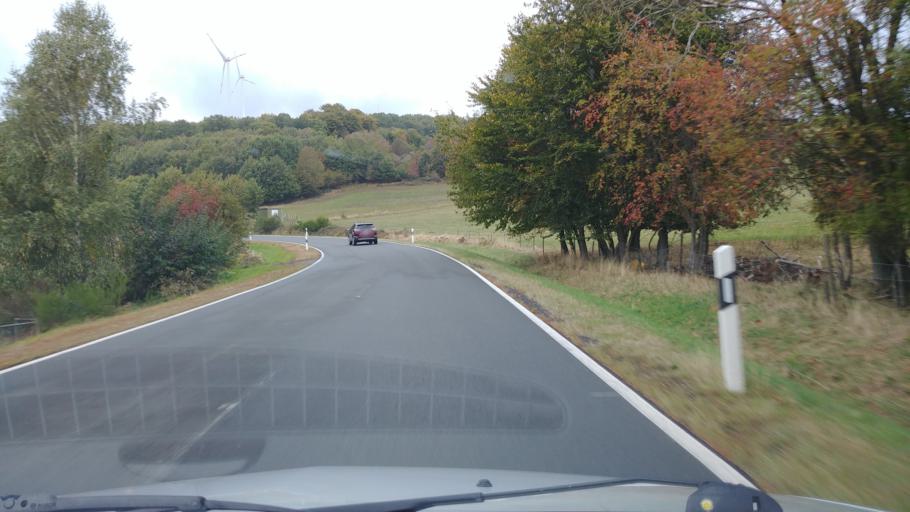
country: DE
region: Rheinland-Pfalz
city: Merschbach
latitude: 49.8212
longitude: 7.0329
